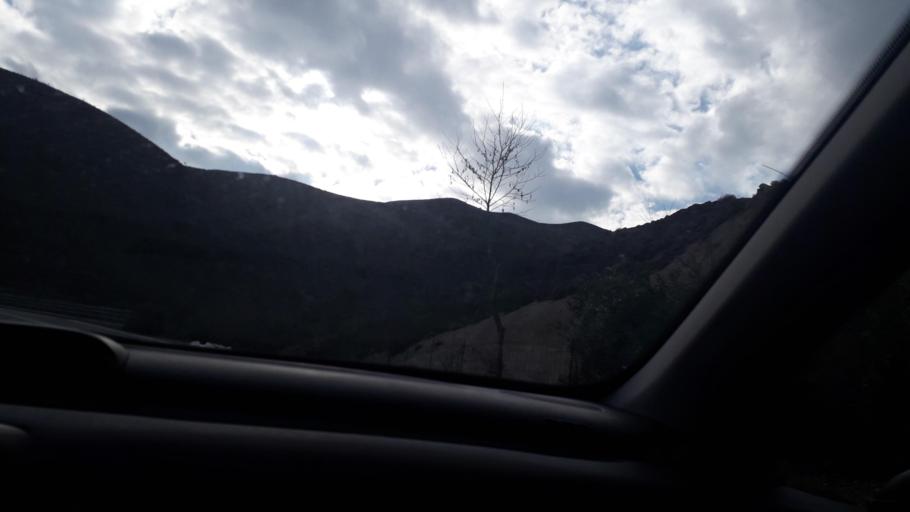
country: GR
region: Crete
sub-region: Nomos Rethymnis
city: Agia Foteini
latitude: 35.2680
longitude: 24.5629
